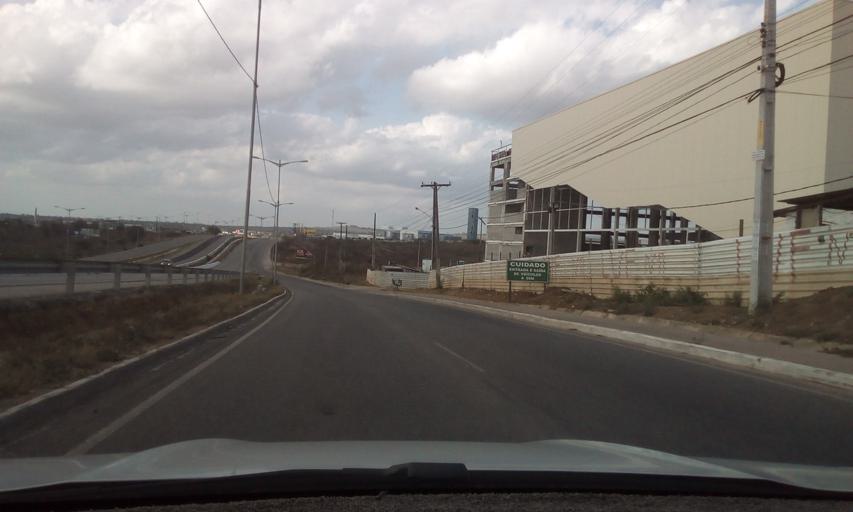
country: BR
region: Pernambuco
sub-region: Caruaru
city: Caruaru
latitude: -8.2513
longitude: -35.9748
